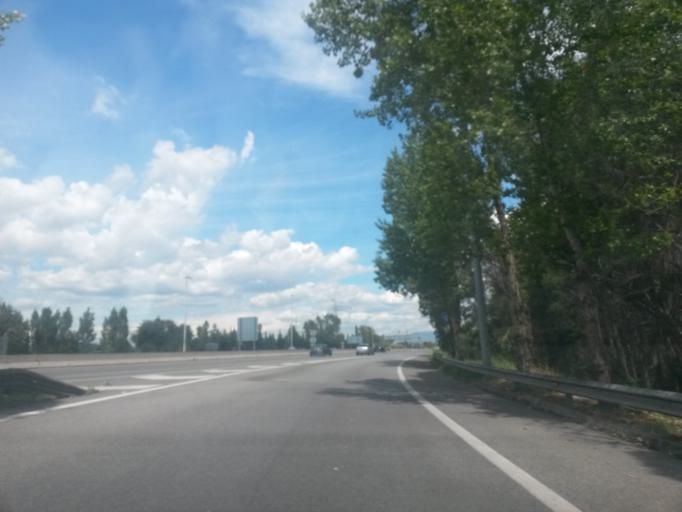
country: ES
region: Catalonia
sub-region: Provincia de Barcelona
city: La Llagosta
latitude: 41.5118
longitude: 2.2060
